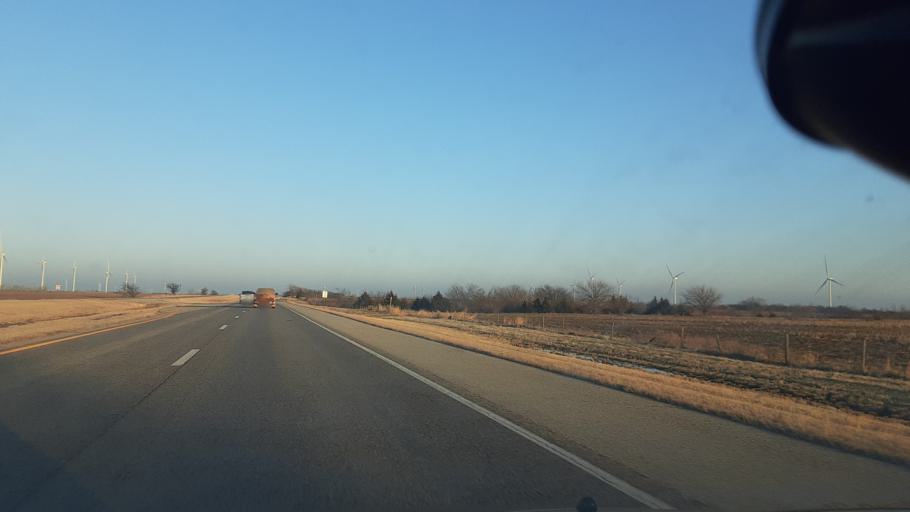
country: US
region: Oklahoma
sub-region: Noble County
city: Perry
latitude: 36.3975
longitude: -97.5250
